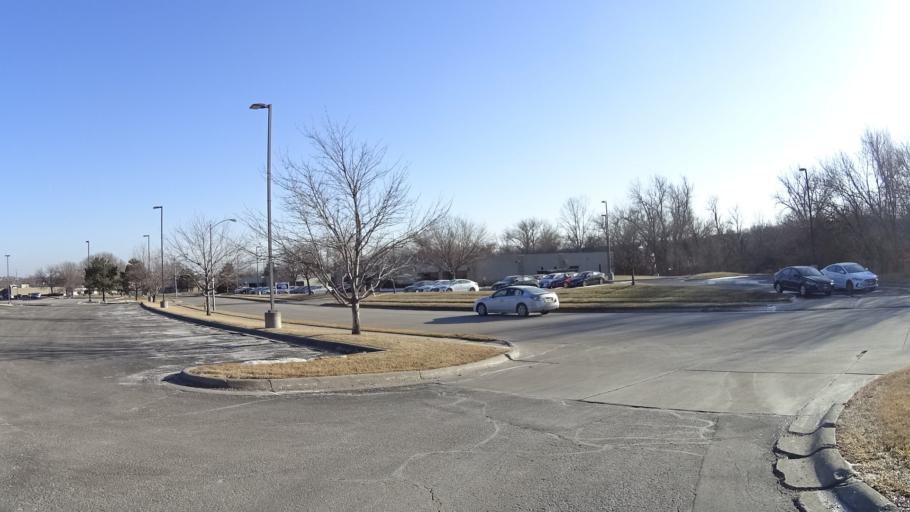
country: US
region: Nebraska
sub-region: Douglas County
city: Bennington
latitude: 41.2914
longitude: -96.1052
